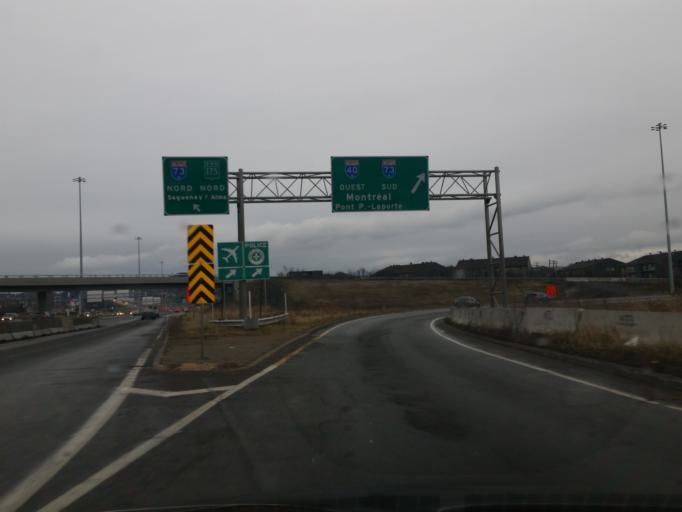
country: CA
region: Quebec
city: Quebec
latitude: 46.8380
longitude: -71.2646
